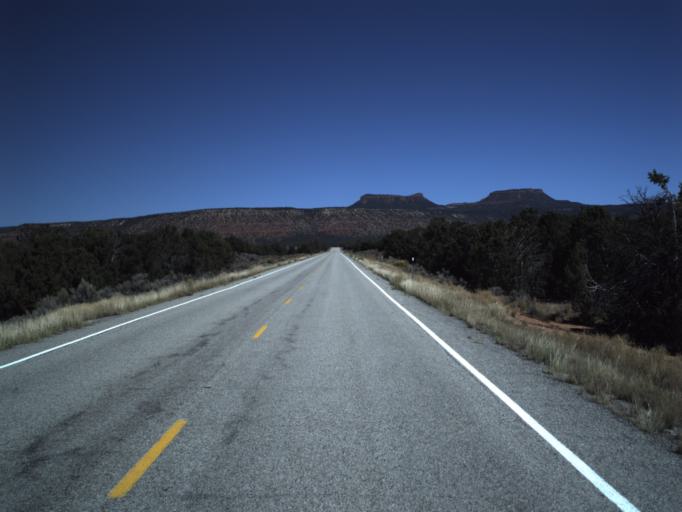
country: US
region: Utah
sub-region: San Juan County
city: Blanding
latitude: 37.5600
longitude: -109.9314
